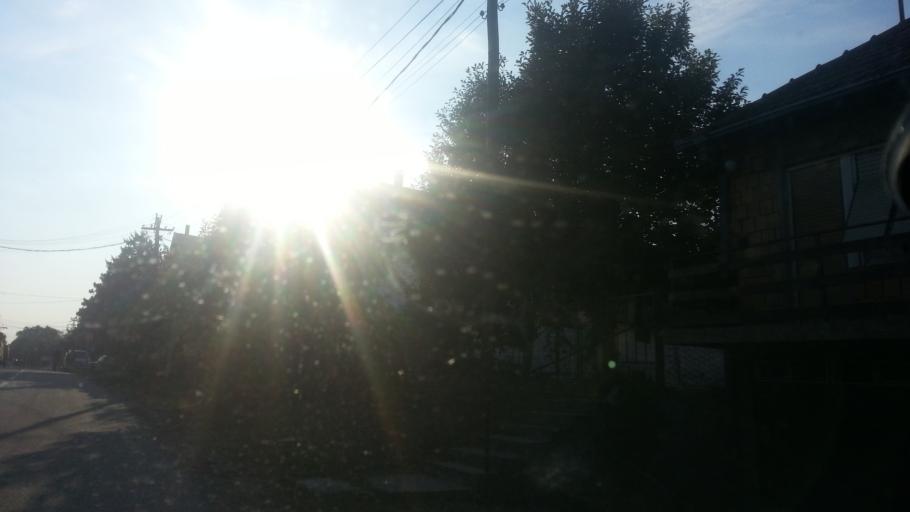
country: RS
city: Novi Slankamen
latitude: 45.1356
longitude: 20.2521
